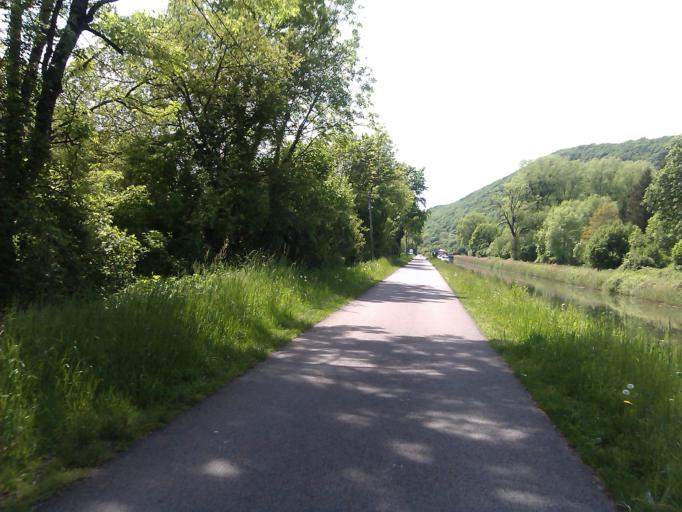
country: FR
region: Franche-Comte
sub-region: Departement du Doubs
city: Avanne-Aveney
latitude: 47.1822
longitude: 5.9544
